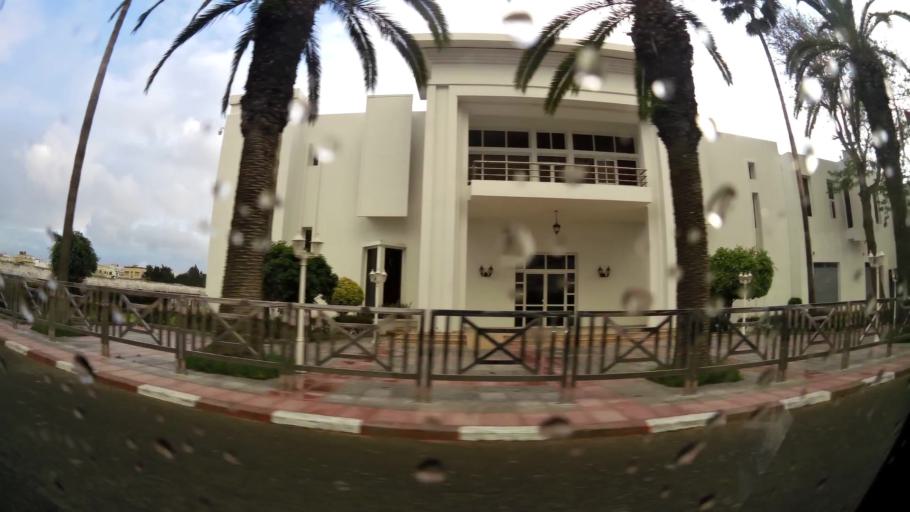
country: MA
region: Doukkala-Abda
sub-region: El-Jadida
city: El Jadida
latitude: 33.2447
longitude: -8.5056
